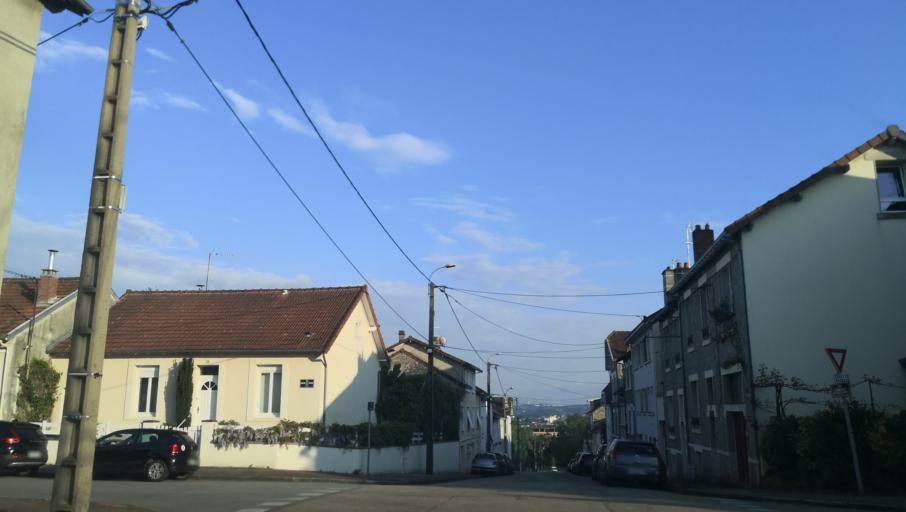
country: FR
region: Limousin
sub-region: Departement de la Haute-Vienne
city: Limoges
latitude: 45.8475
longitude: 1.2517
